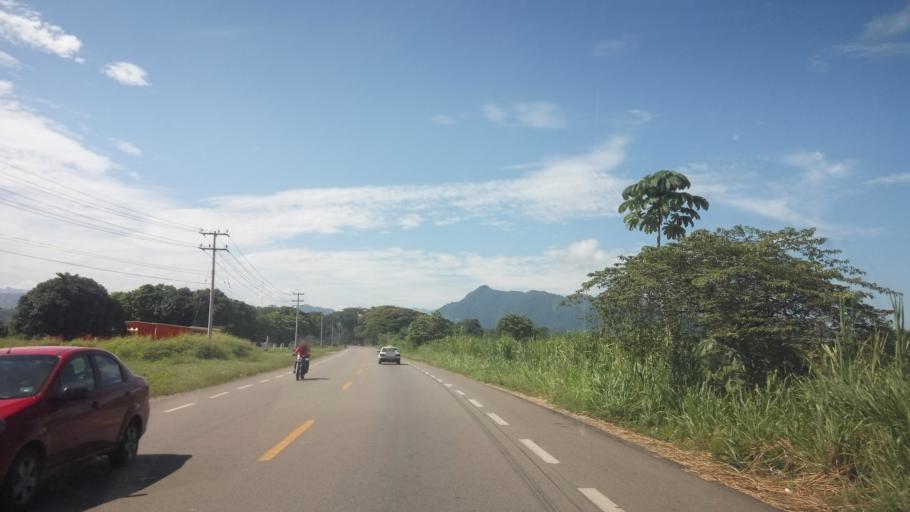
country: MX
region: Tabasco
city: Teapa
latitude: 17.5867
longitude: -92.9674
